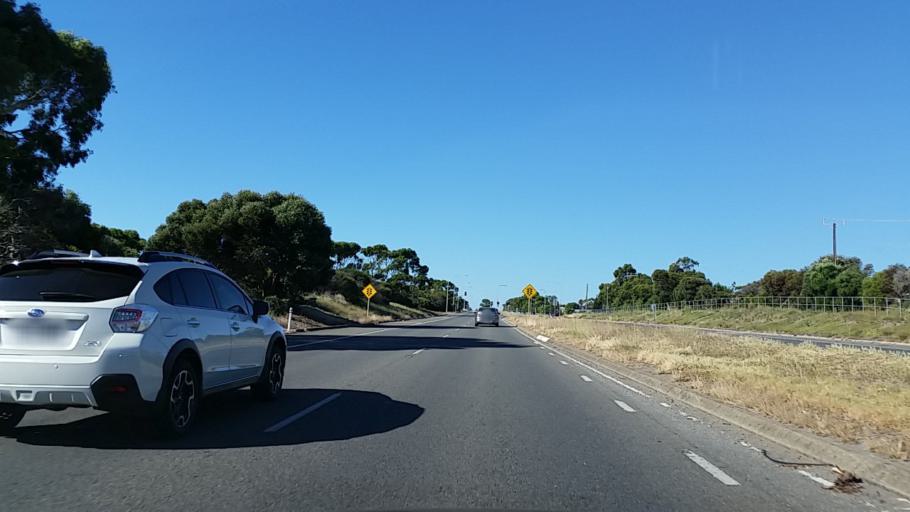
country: AU
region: South Australia
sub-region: Marion
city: Happy Valley
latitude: -35.0740
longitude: 138.5233
